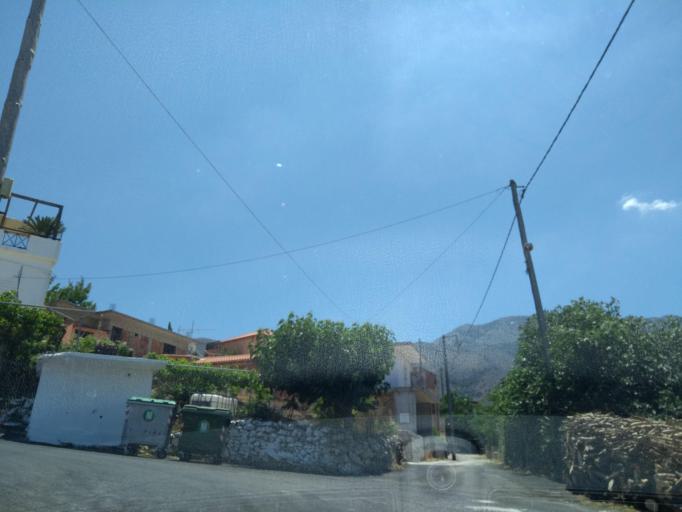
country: GR
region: Crete
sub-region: Nomos Chanias
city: Georgioupolis
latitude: 35.3141
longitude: 24.3095
